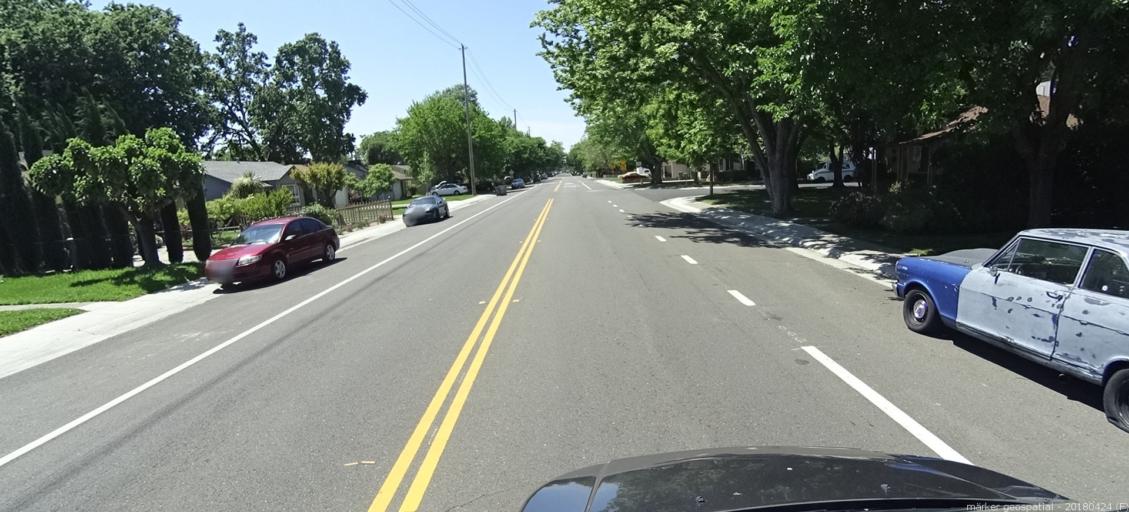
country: US
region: California
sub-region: Yolo County
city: West Sacramento
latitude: 38.5837
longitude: -121.5322
